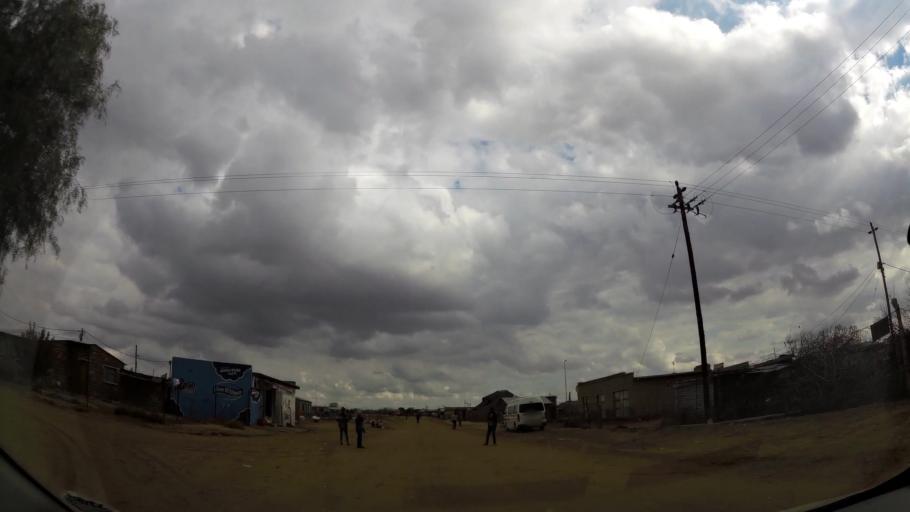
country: ZA
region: Orange Free State
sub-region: Fezile Dabi District Municipality
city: Sasolburg
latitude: -26.8597
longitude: 27.8664
